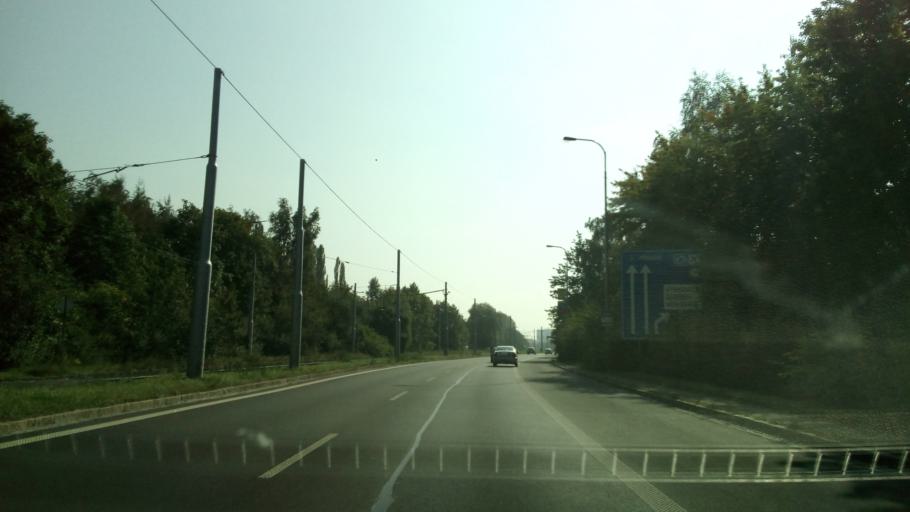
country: CZ
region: Moravskoslezsky
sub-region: Okres Ostrava-Mesto
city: Ostrava
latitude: 49.8100
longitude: 18.2436
